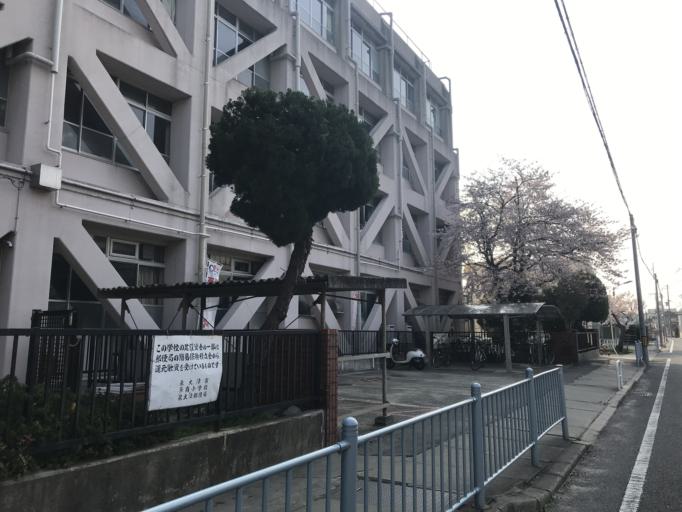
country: JP
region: Osaka
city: Izumiotsu
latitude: 34.5005
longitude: 135.4196
